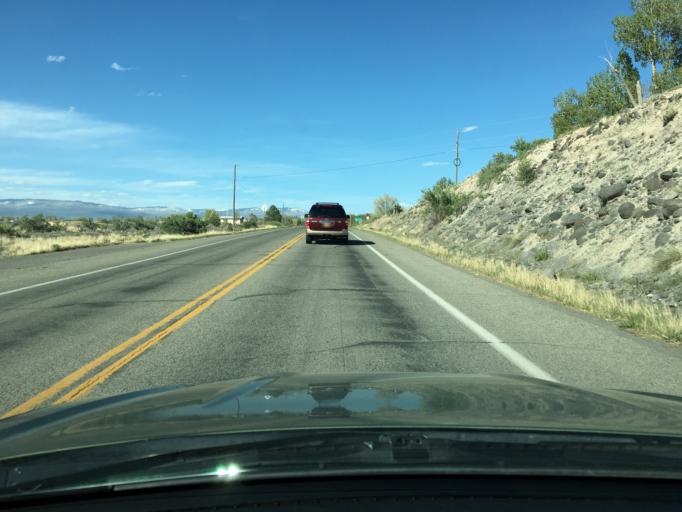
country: US
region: Colorado
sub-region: Delta County
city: Orchard City
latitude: 38.7841
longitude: -107.9955
